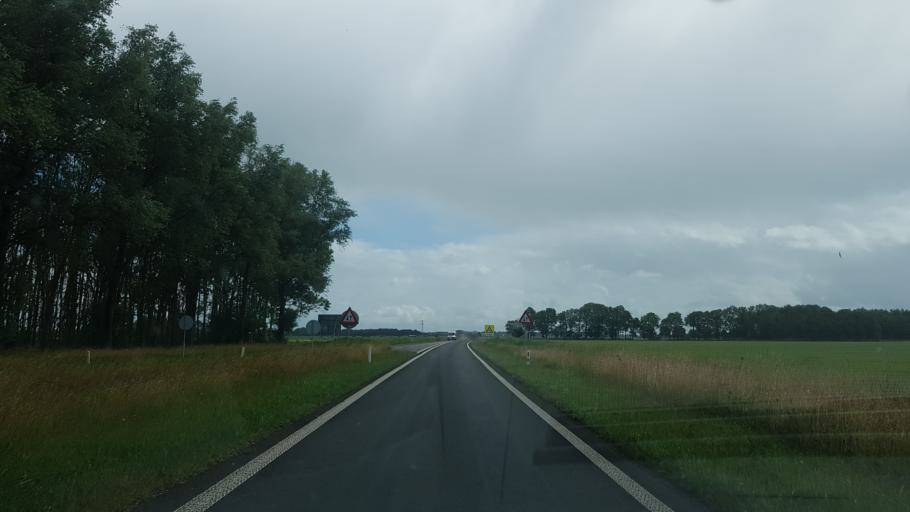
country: NL
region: Friesland
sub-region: Gemeente Dantumadiel
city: Rinsumageast
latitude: 53.3017
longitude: 5.9488
